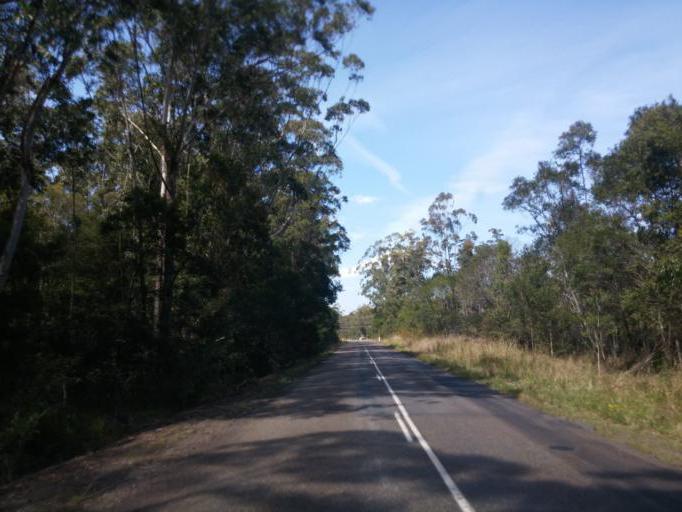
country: AU
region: New South Wales
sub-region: Great Lakes
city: Bulahdelah
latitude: -32.3937
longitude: 152.2524
